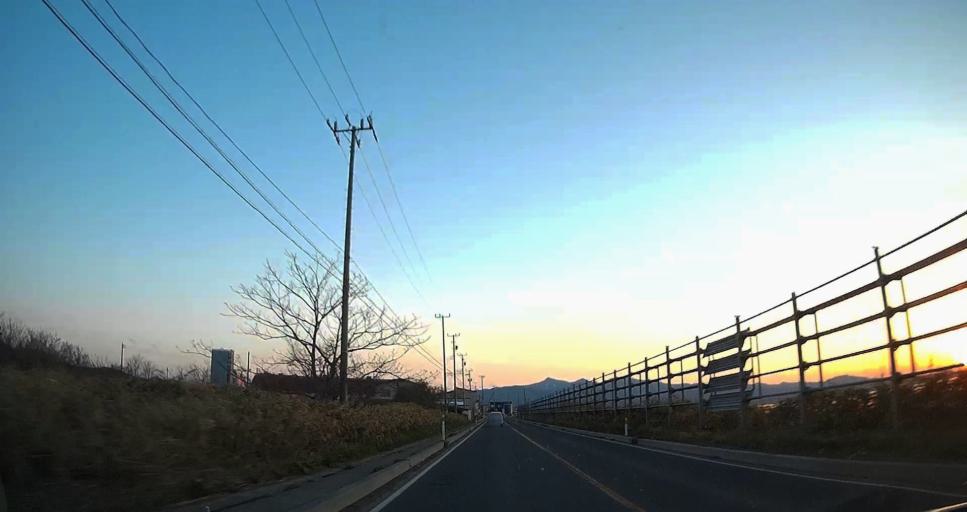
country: JP
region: Aomori
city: Misawa
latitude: 40.8782
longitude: 141.1472
